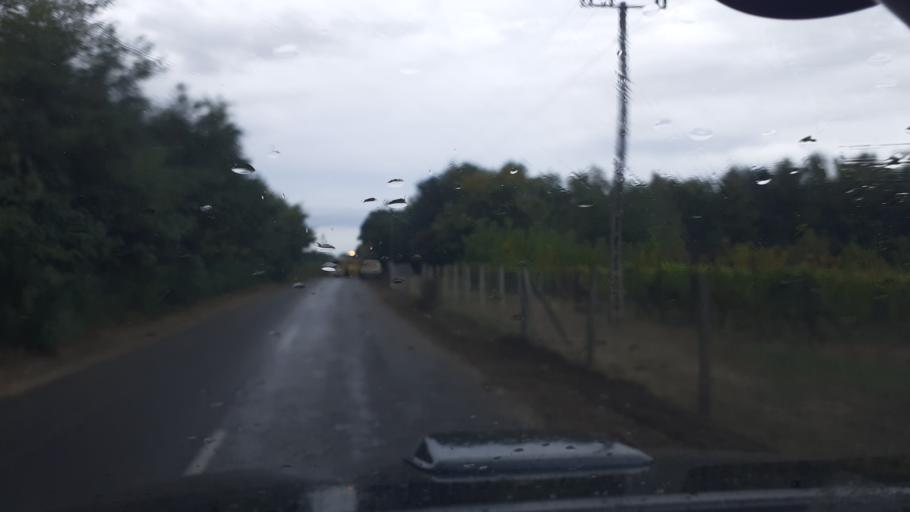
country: HU
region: Tolna
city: Bolcske
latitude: 46.7548
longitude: 18.9630
